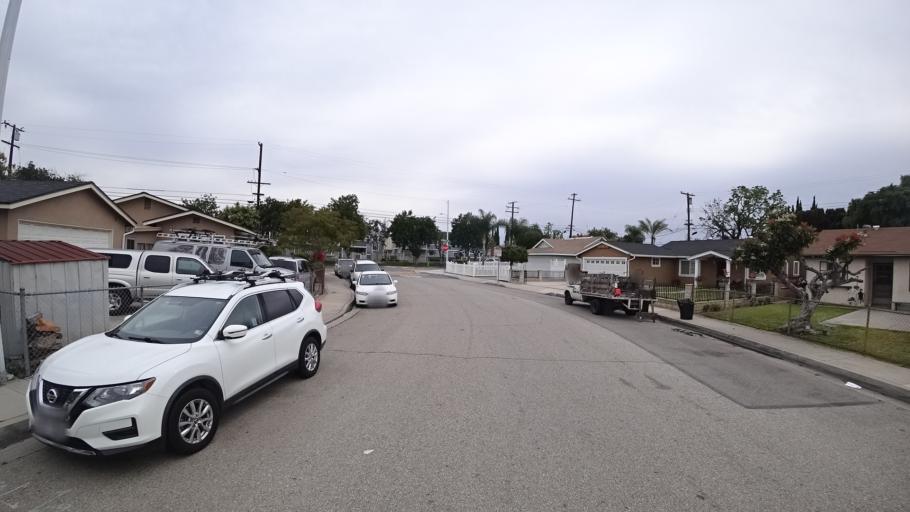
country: US
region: California
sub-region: Los Angeles County
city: West Puente Valley
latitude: 34.0698
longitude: -117.9844
